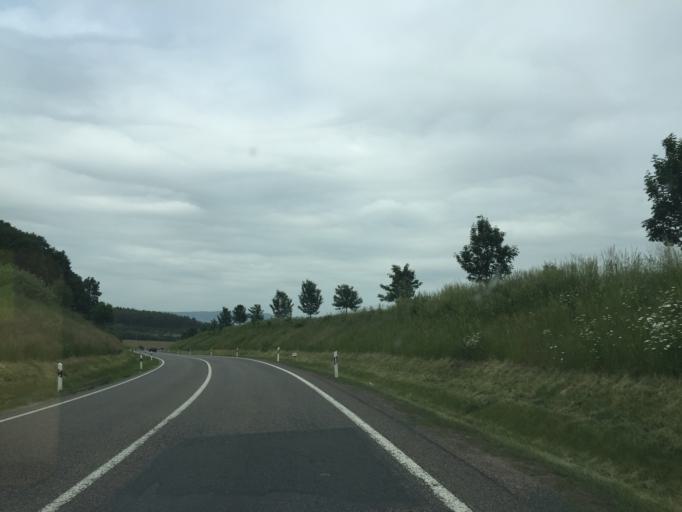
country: DE
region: Thuringia
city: Langewiesen
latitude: 50.7076
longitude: 10.9646
